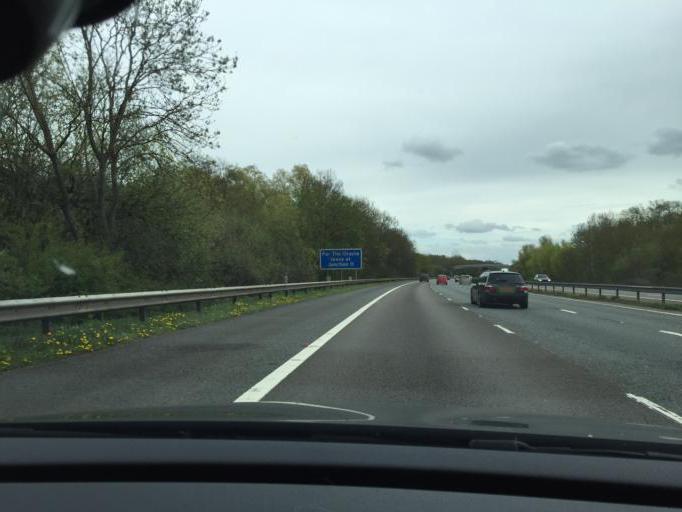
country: GB
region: England
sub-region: West Berkshire
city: Theale
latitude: 51.4545
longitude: -1.0826
